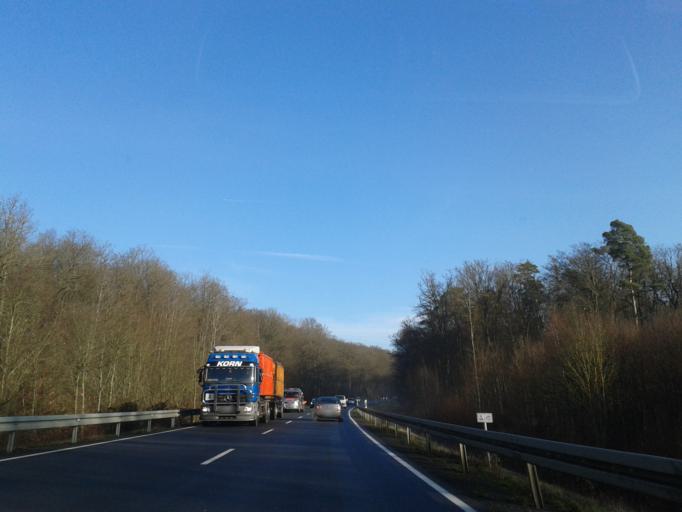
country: DE
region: Bavaria
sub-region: Regierungsbezirk Unterfranken
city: Aidhausen
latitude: 50.1081
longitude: 10.4172
